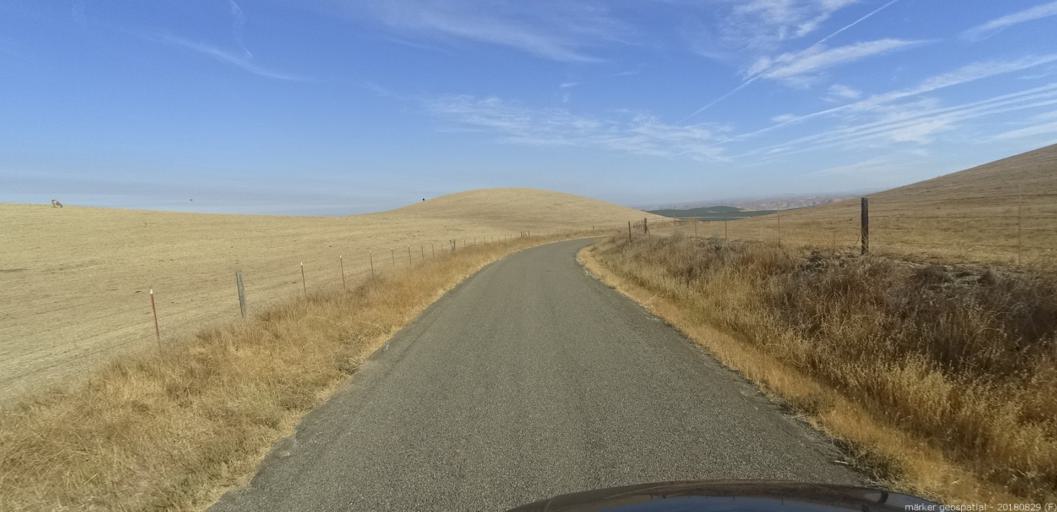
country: US
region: California
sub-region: Monterey County
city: King City
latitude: 36.0464
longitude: -120.9773
